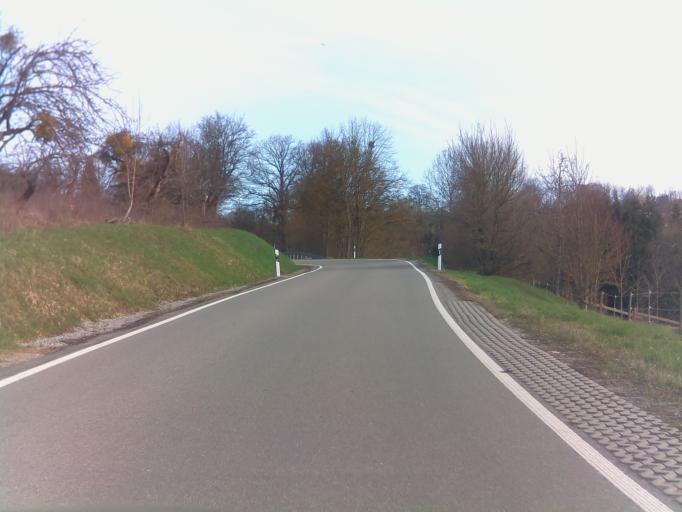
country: DE
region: Baden-Wuerttemberg
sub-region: Regierungsbezirk Stuttgart
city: Oppenweiler
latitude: 48.9912
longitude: 9.4563
